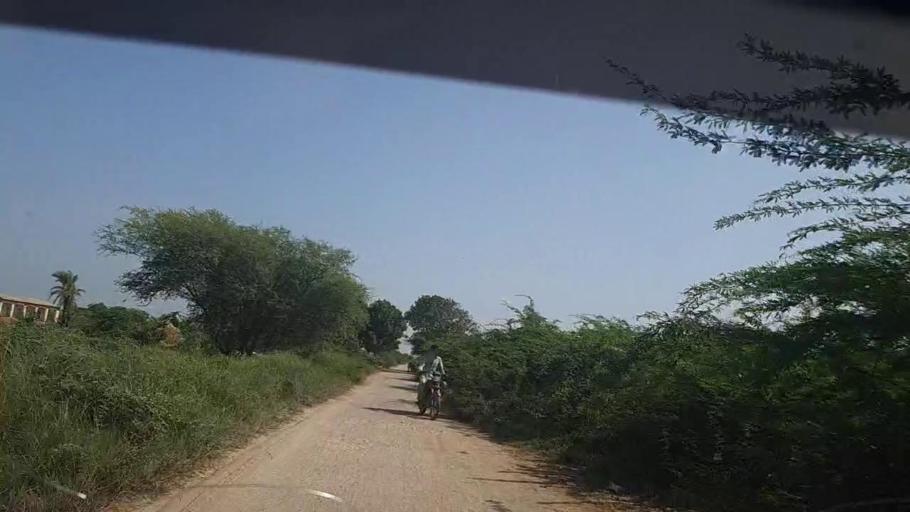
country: PK
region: Sindh
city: Rajo Khanani
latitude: 24.9727
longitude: 68.8699
